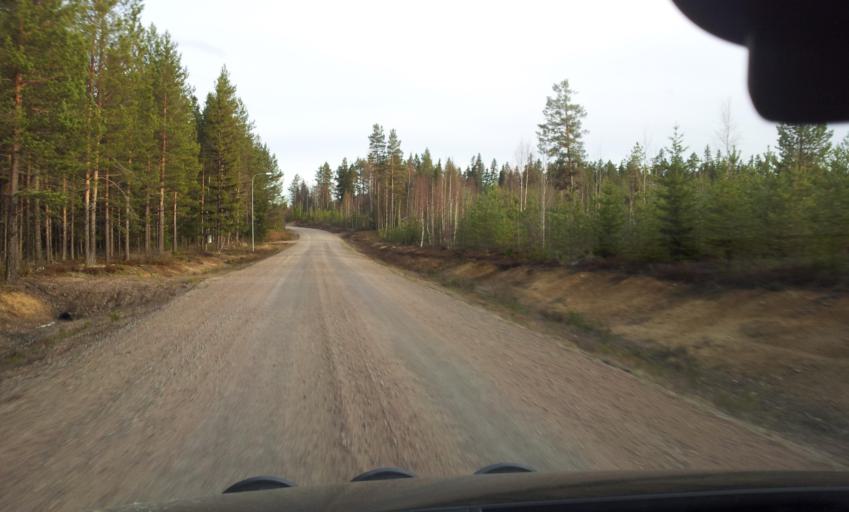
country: SE
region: Gaevleborg
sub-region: Ljusdals Kommun
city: Farila
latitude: 62.1338
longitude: 15.6614
